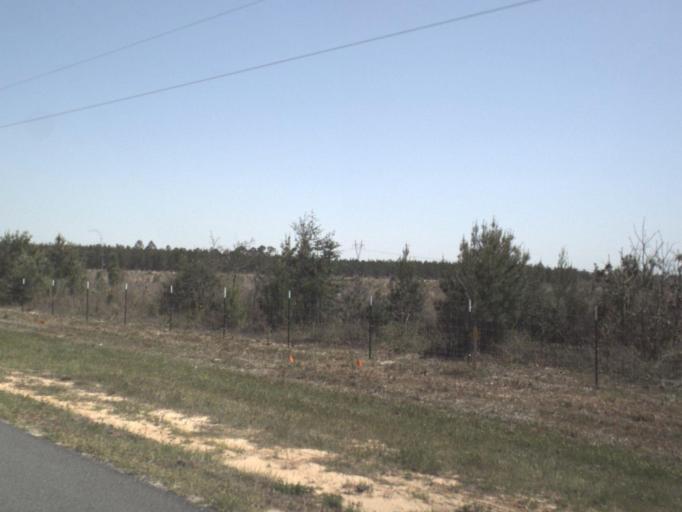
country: US
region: Florida
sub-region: Bay County
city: Youngstown
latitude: 30.4352
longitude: -85.3578
